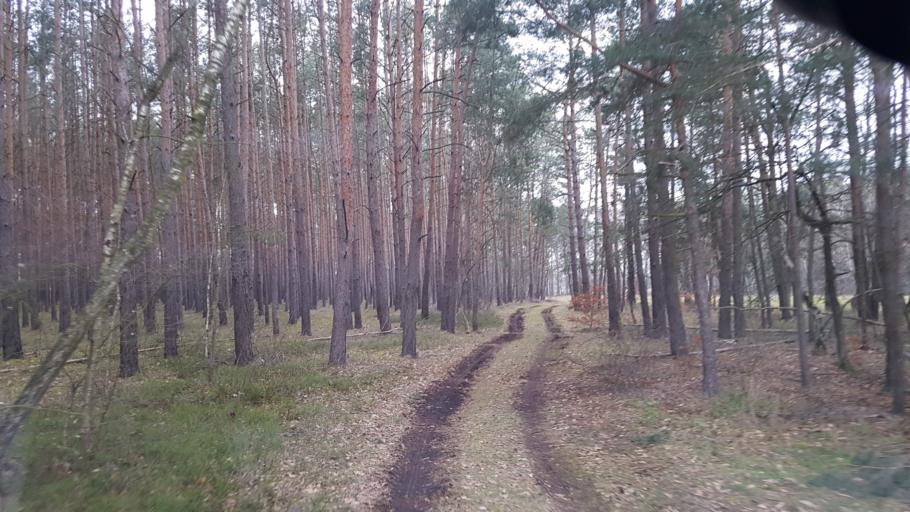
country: DE
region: Brandenburg
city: Schonborn
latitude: 51.6033
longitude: 13.5071
